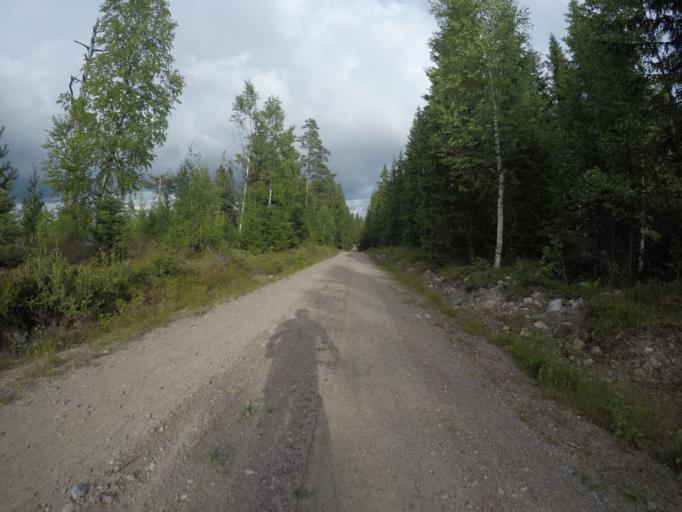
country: SE
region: Vaermland
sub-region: Filipstads Kommun
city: Lesjofors
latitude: 60.1998
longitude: 14.3383
